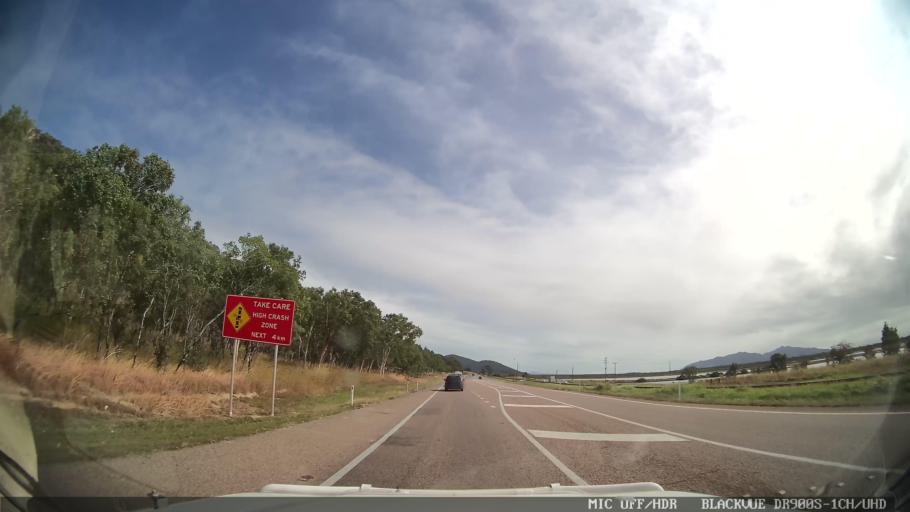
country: AU
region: Queensland
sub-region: Townsville
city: Townsville
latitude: -19.3980
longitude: 147.0230
